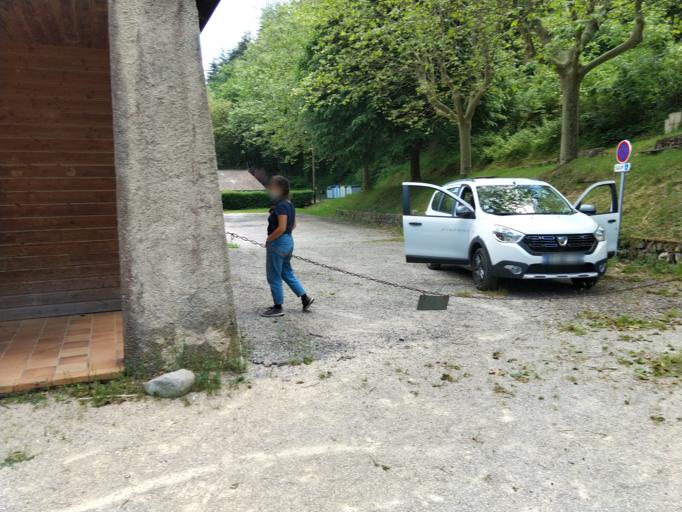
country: FR
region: Rhone-Alpes
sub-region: Departement de l'Ardeche
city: Saint-Sauveur-de-Montagut
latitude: 44.8131
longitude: 4.4828
